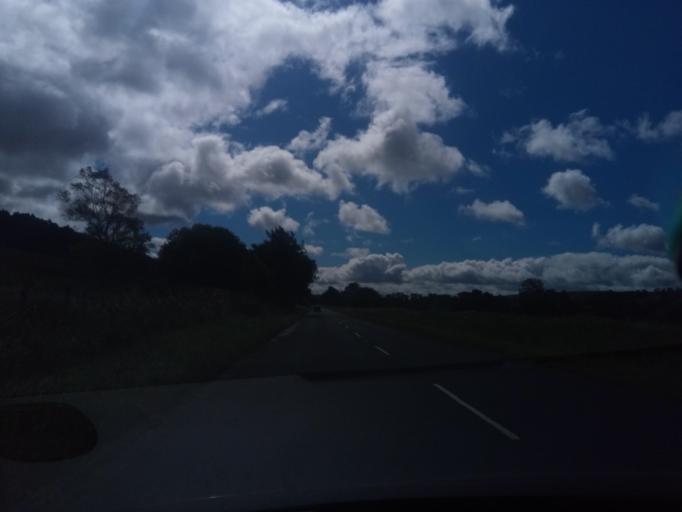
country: GB
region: England
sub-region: Northumberland
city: Rochester
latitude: 55.2870
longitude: -2.2934
